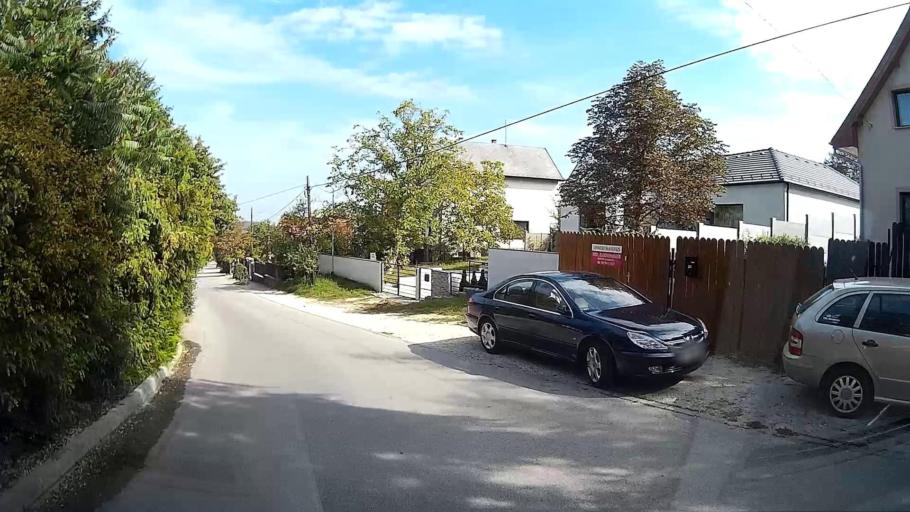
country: HU
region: Pest
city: Solymar
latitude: 47.5902
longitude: 18.9233
